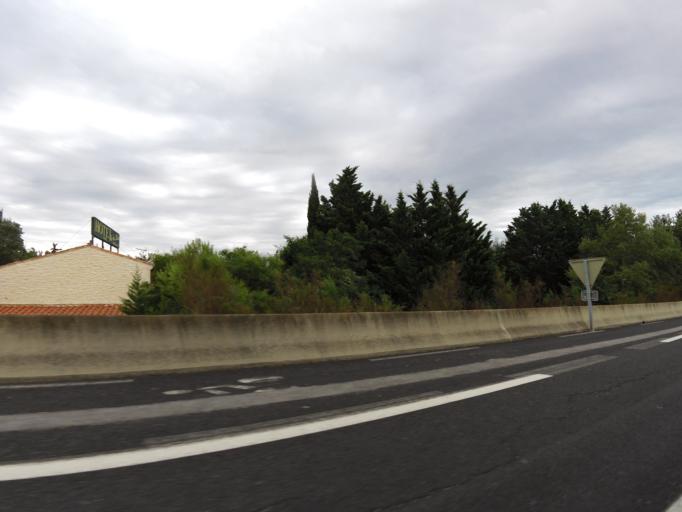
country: FR
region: Languedoc-Roussillon
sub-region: Departement du Gard
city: Aigues-Mortes
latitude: 43.5862
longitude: 4.1967
